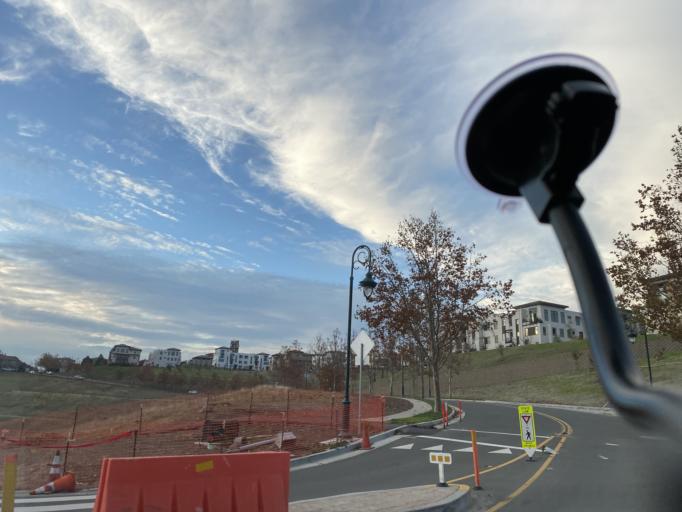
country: US
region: California
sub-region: Santa Clara County
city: Seven Trees
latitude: 37.2820
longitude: -121.8511
